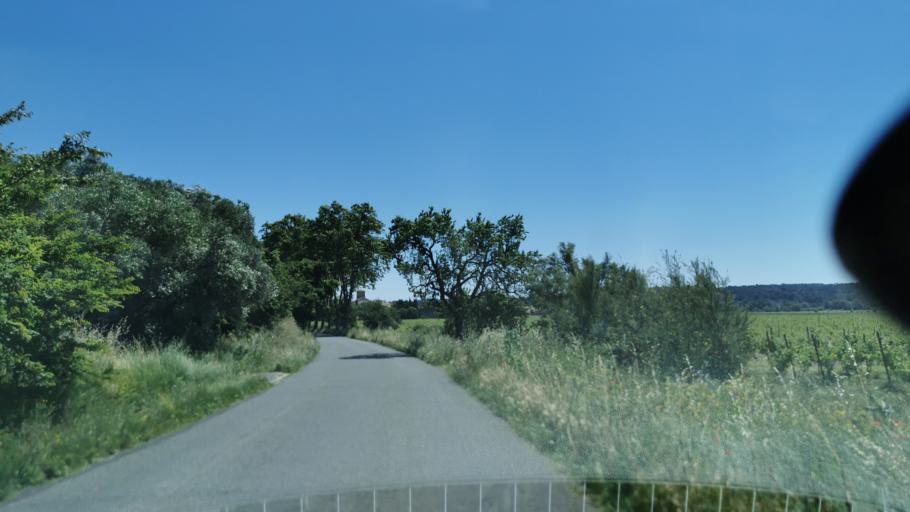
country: FR
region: Languedoc-Roussillon
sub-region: Departement de l'Aude
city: Marcorignan
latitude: 43.2431
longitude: 2.9154
